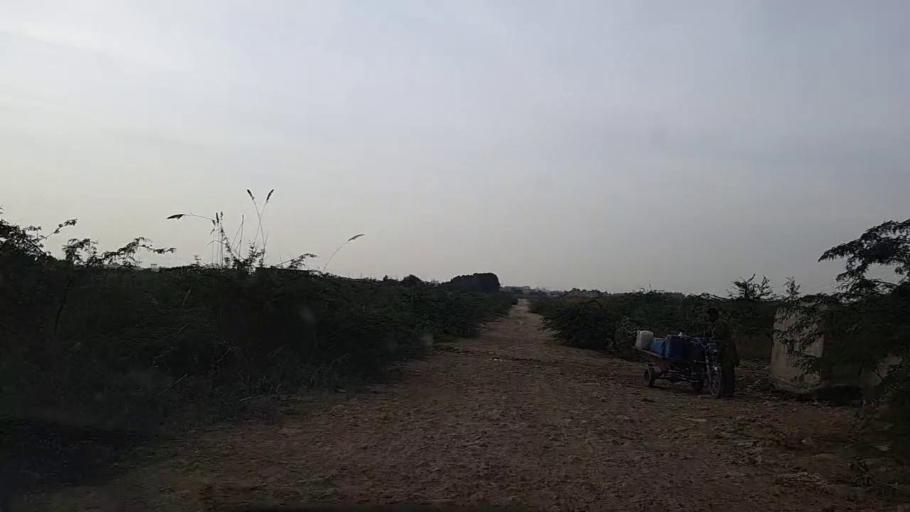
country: PK
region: Sindh
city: Gharo
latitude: 24.7942
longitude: 67.5415
